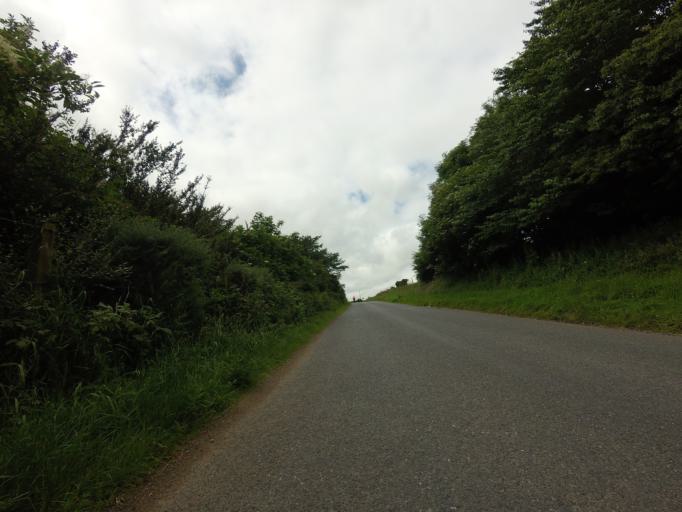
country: GB
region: Scotland
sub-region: Aberdeenshire
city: Rosehearty
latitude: 57.5373
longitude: -2.1872
